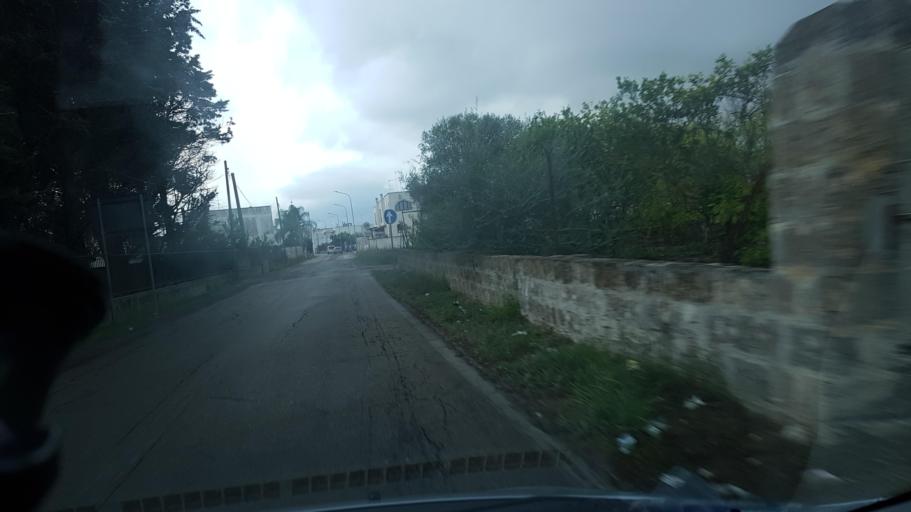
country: IT
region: Apulia
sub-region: Provincia di Lecce
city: Carmiano
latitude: 40.3510
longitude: 18.0517
